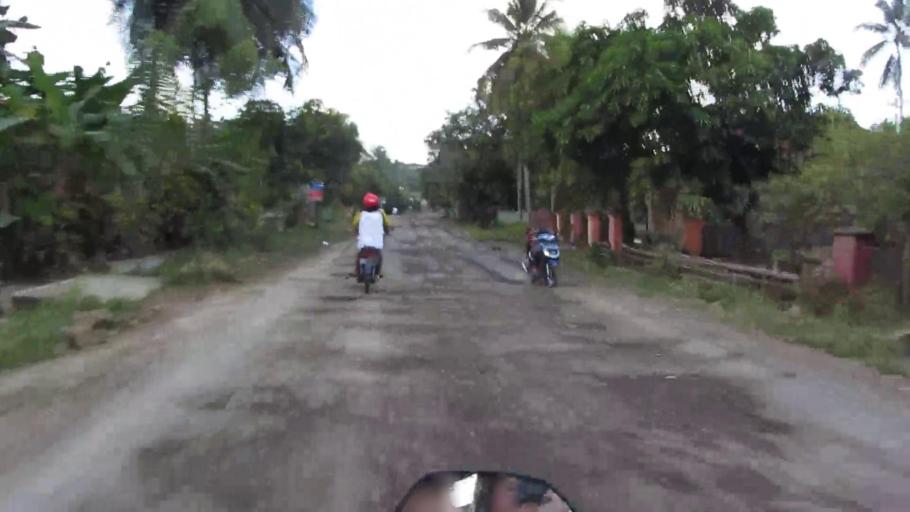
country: ID
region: West Java
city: Binangun
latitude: -7.7156
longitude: 108.4777
